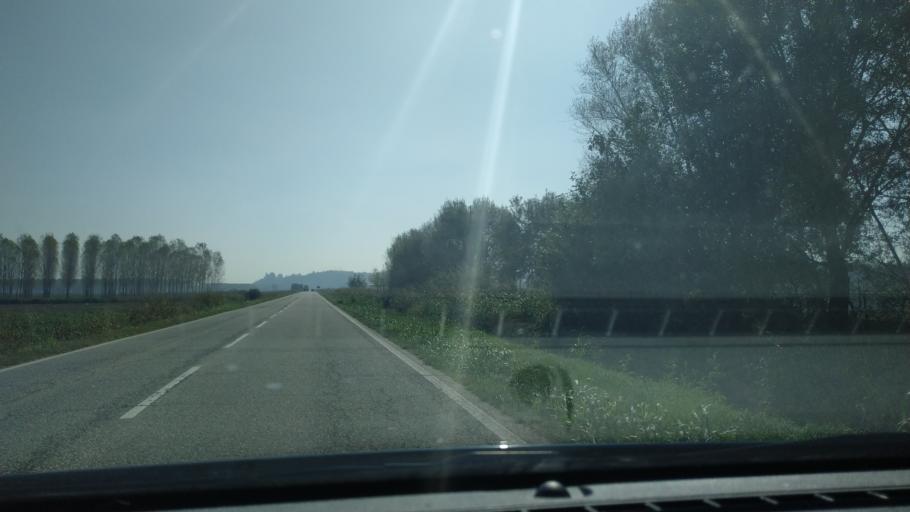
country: IT
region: Piedmont
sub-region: Provincia di Alessandria
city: Giarole
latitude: 45.0782
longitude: 8.5679
